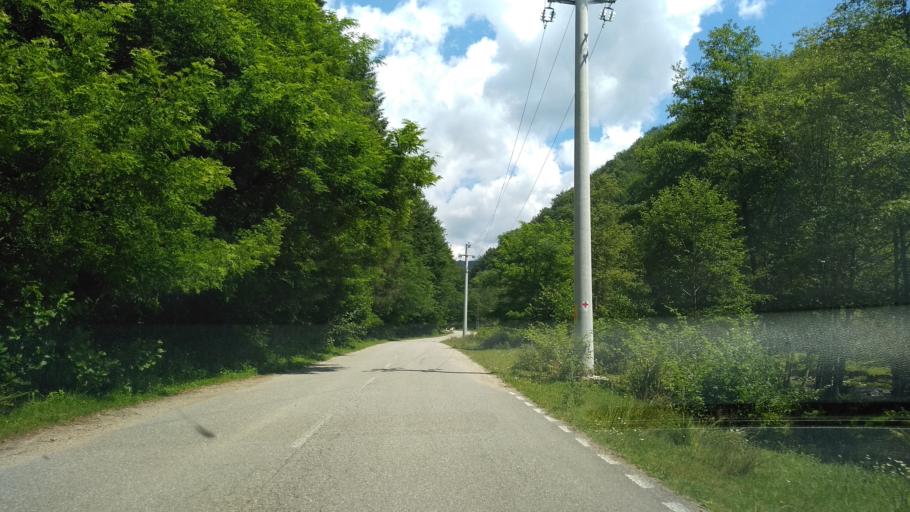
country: RO
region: Hunedoara
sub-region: Comuna Orastioara de Sus
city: Orastioara de Sus
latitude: 45.6235
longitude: 23.2561
